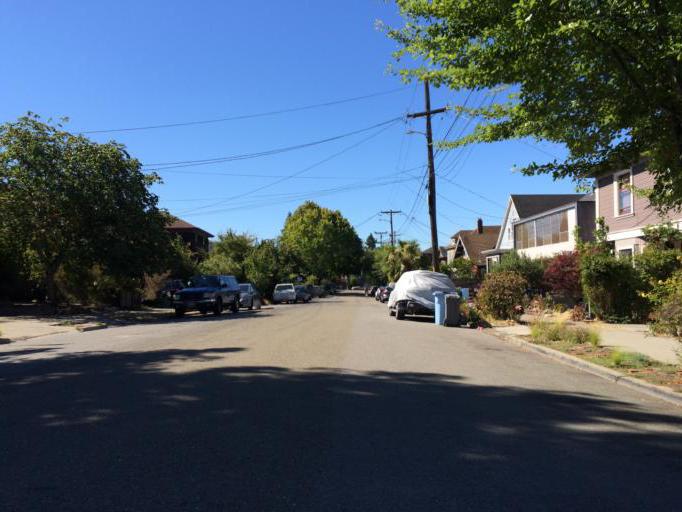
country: US
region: California
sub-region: Alameda County
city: Berkeley
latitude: 37.8771
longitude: -122.2748
